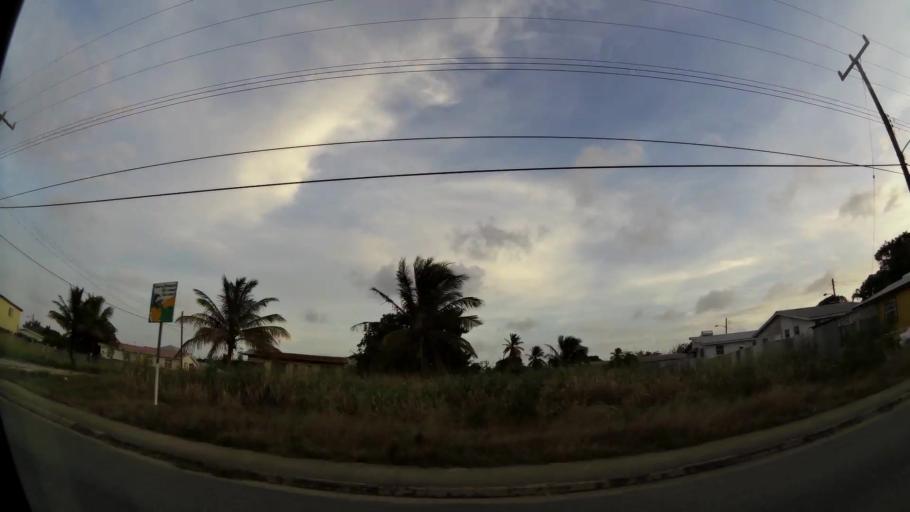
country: BB
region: Saint Philip
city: Crane
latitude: 13.0992
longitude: -59.4972
